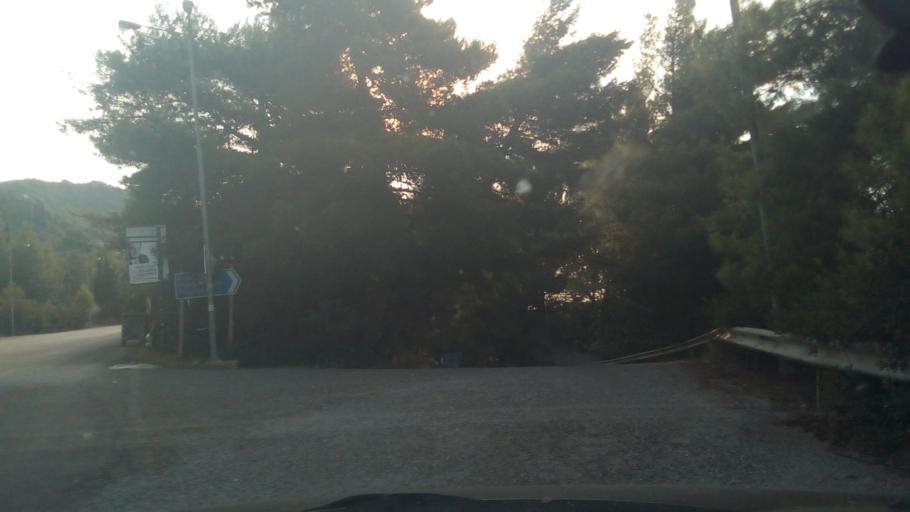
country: GR
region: West Greece
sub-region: Nomos Aitolias kai Akarnanias
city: Nafpaktos
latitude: 38.4083
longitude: 21.9455
